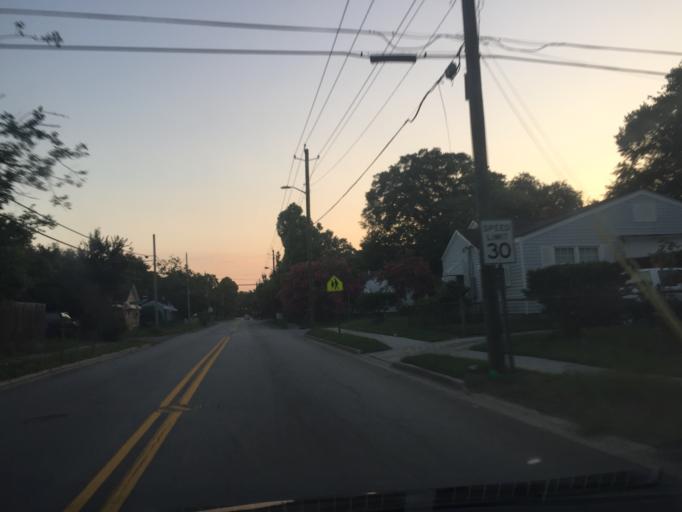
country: US
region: Georgia
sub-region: Chatham County
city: Thunderbolt
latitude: 32.0665
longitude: -81.0585
